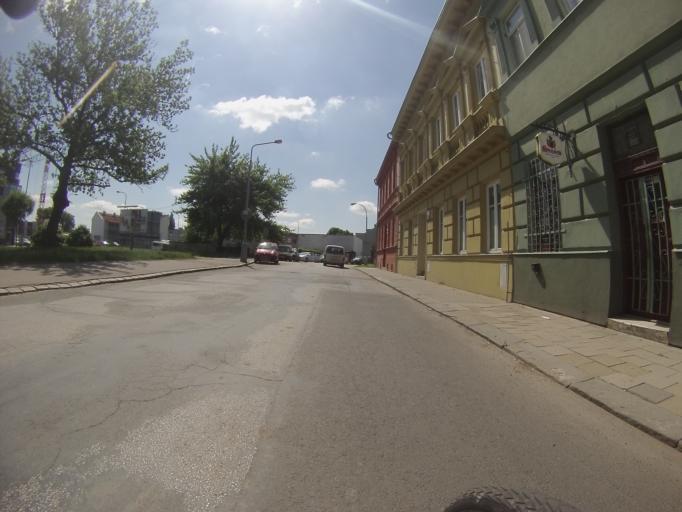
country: CZ
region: South Moravian
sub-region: Mesto Brno
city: Brno
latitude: 49.1823
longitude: 16.6194
